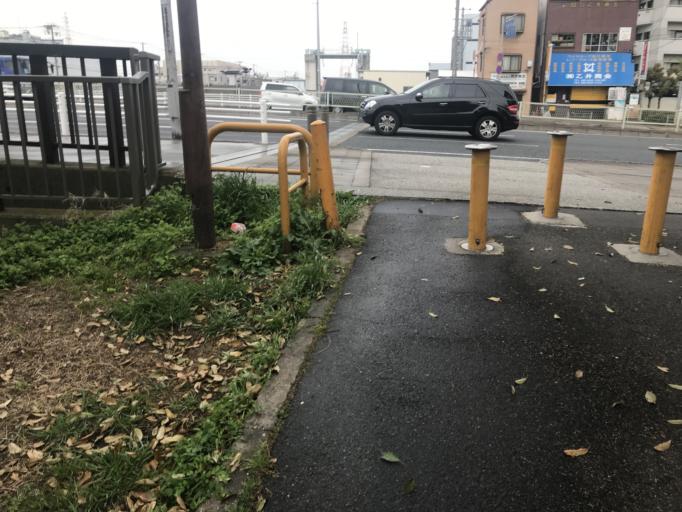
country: JP
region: Osaka
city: Sakai
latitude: 34.6145
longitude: 135.4738
